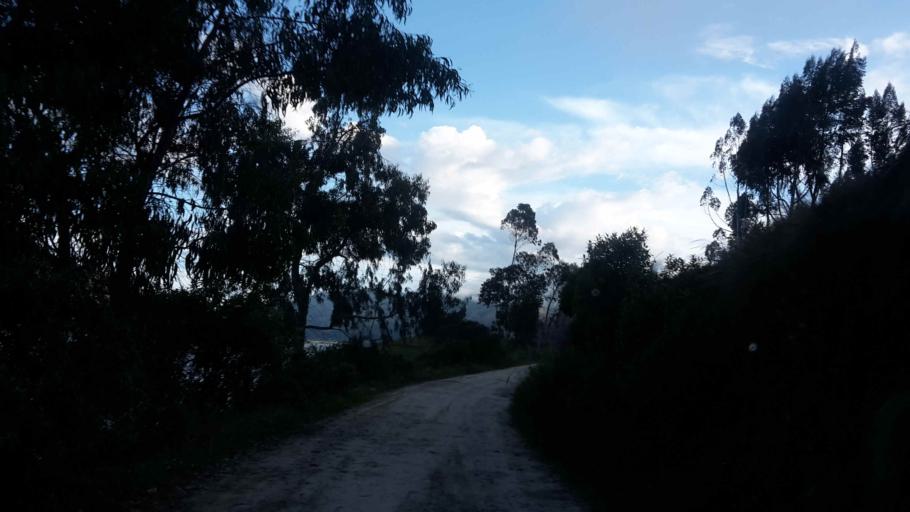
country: BO
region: Cochabamba
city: Colomi
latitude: -17.2650
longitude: -65.9066
